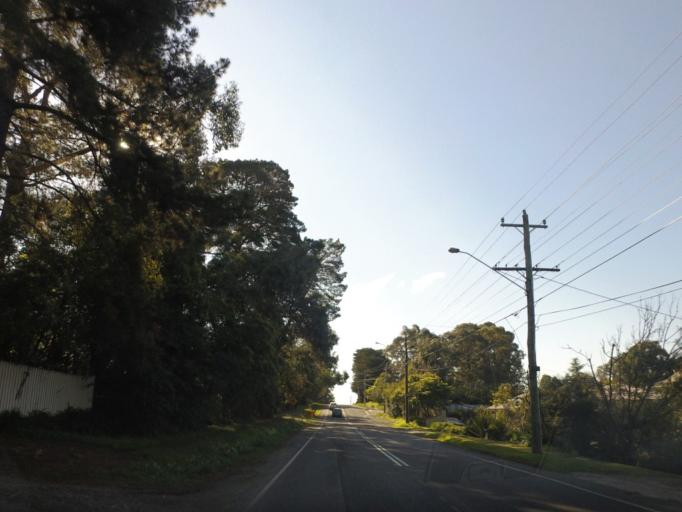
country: AU
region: Victoria
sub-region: Manningham
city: Donvale
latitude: -37.7887
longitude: 145.1806
